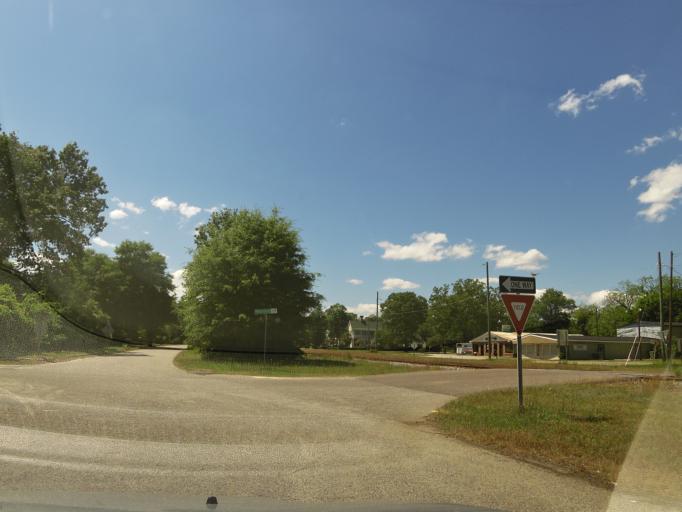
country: US
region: South Carolina
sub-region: Aiken County
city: Aiken
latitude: 33.5548
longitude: -81.7092
